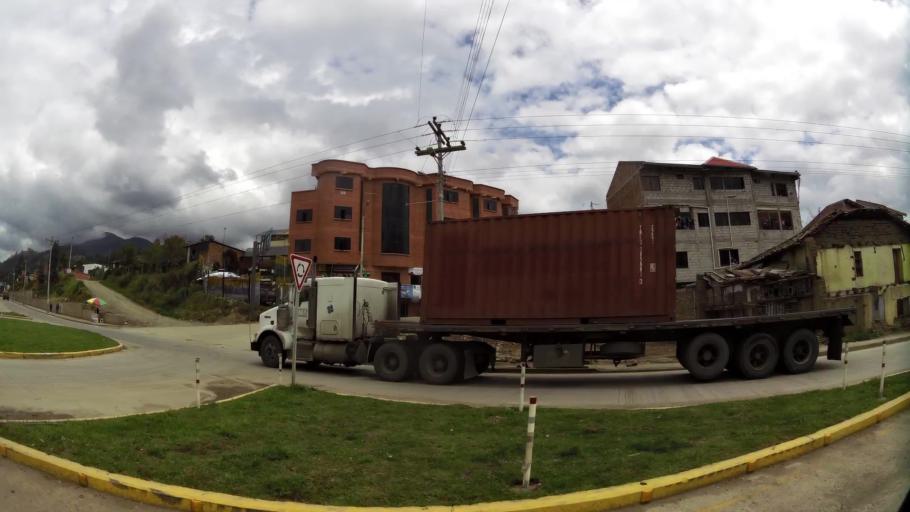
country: EC
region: Azuay
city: Cuenca
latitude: -2.8801
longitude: -79.0667
